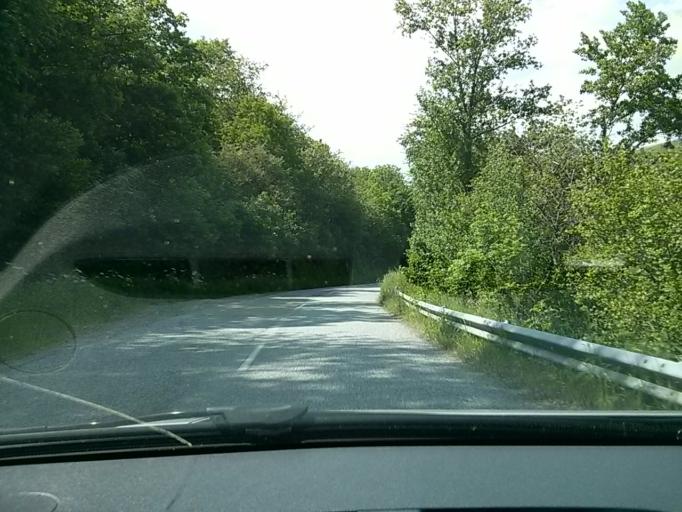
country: FR
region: Rhone-Alpes
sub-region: Departement de la Loire
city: Saint-Chamond
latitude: 45.4219
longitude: 4.5290
